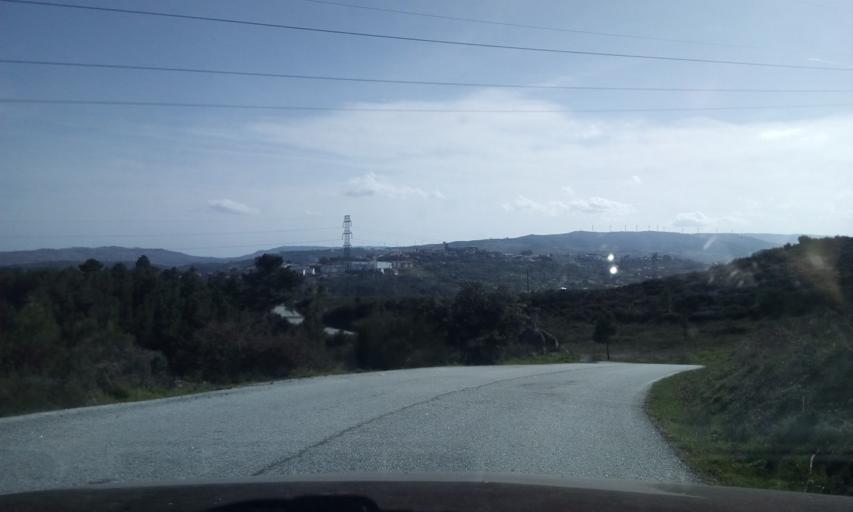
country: PT
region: Guarda
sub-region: Celorico da Beira
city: Celorico da Beira
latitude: 40.6538
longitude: -7.3986
